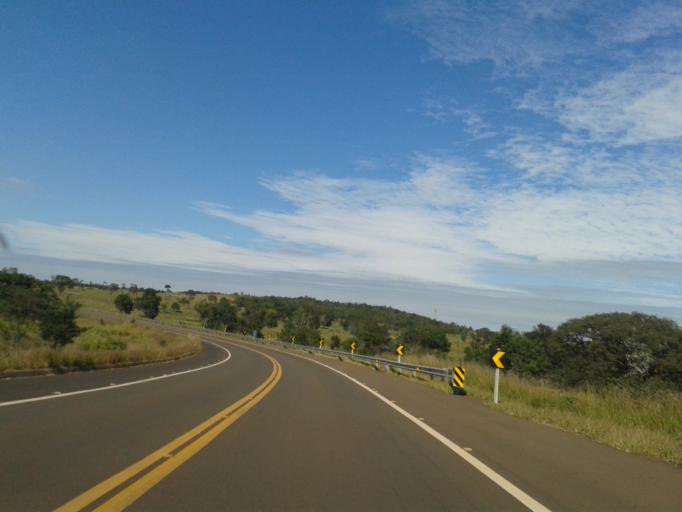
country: BR
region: Minas Gerais
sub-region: Campina Verde
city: Campina Verde
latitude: -19.4316
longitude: -49.5796
